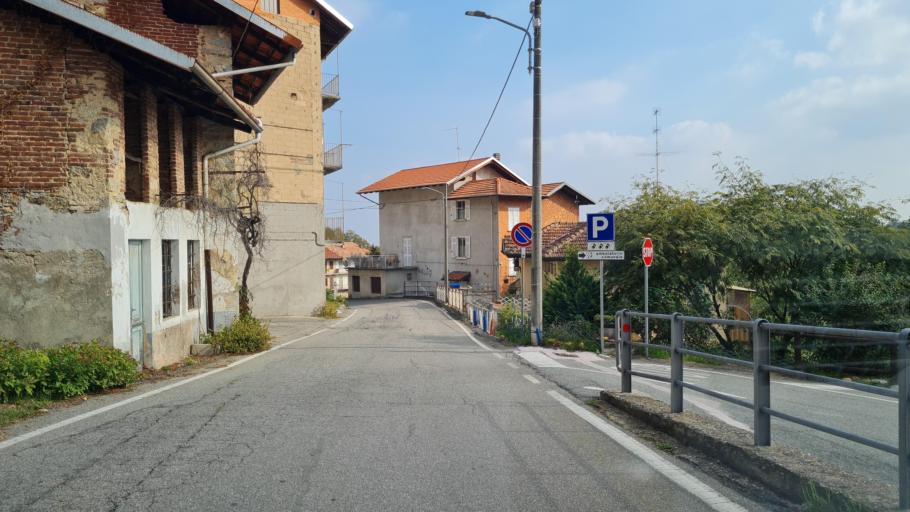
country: IT
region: Piedmont
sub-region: Provincia di Biella
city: Mezzana Mortigliengo
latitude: 45.6266
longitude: 8.1905
